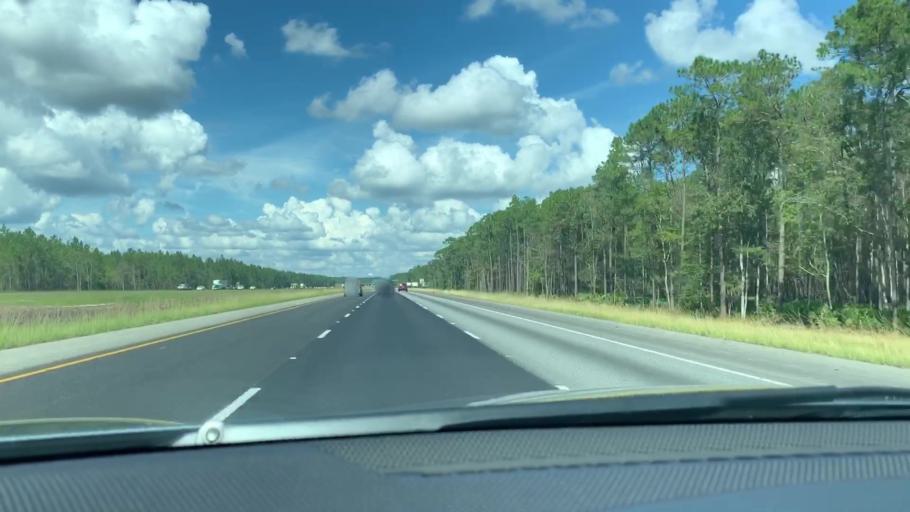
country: US
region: Georgia
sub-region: Camden County
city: Woodbine
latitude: 30.9268
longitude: -81.6858
